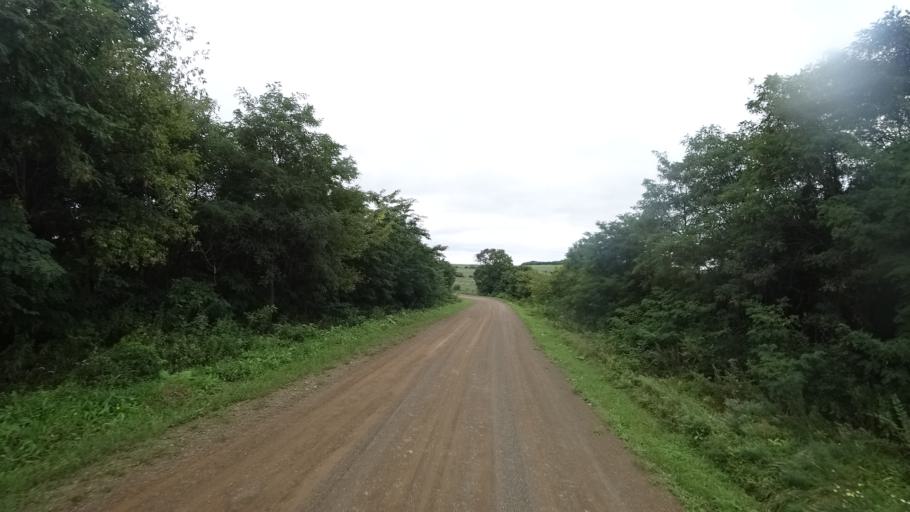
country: RU
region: Primorskiy
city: Chernigovka
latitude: 44.4537
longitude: 132.5841
